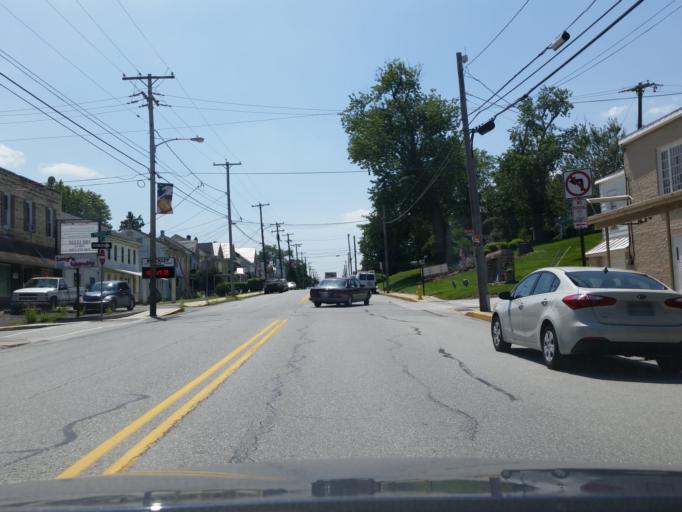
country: US
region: Pennsylvania
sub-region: York County
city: Hallam
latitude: 40.0051
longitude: -76.6041
